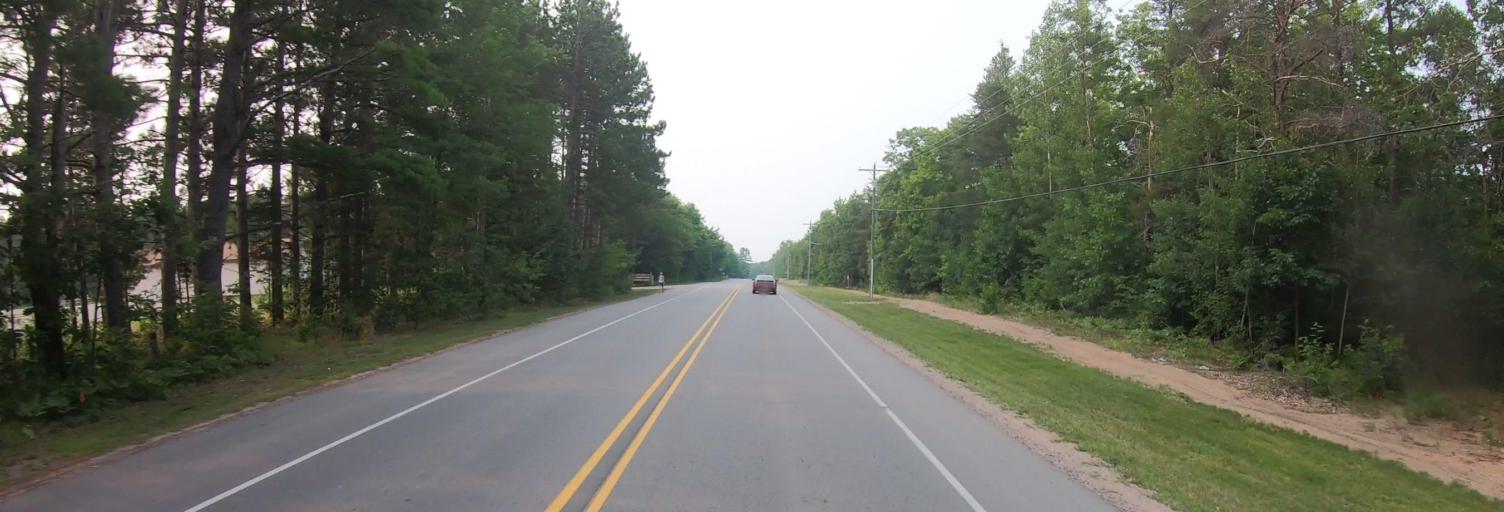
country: US
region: Michigan
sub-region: Chippewa County
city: Sault Ste. Marie
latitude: 46.4639
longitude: -84.6192
